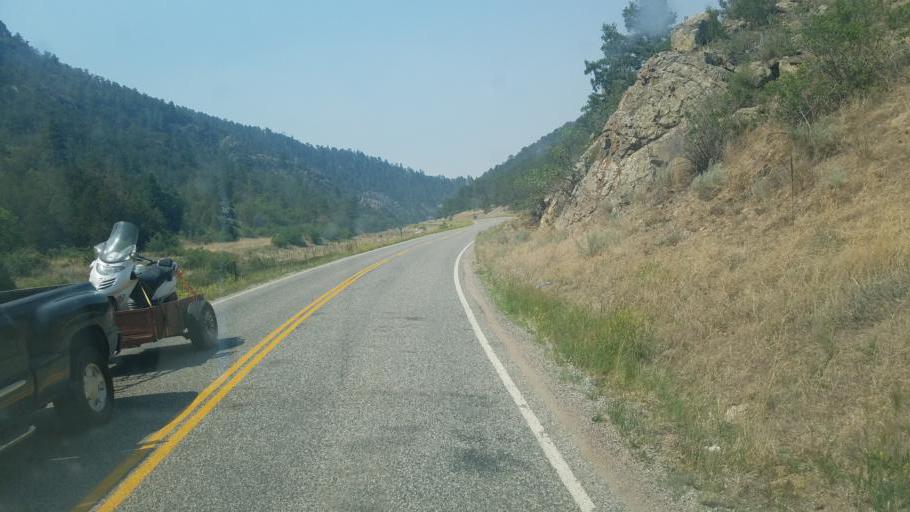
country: US
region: Colorado
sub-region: Fremont County
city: Canon City
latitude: 38.3953
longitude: -105.4473
